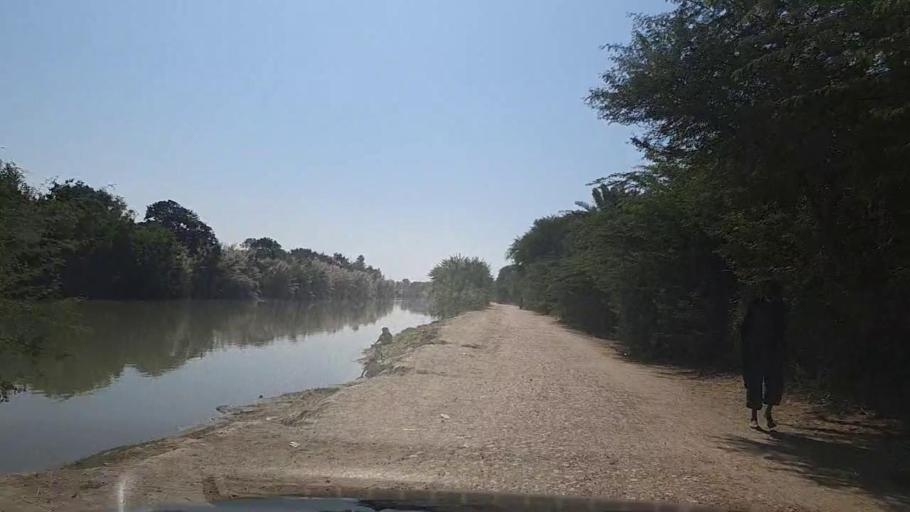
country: PK
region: Sindh
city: Thatta
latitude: 24.5992
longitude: 67.8202
